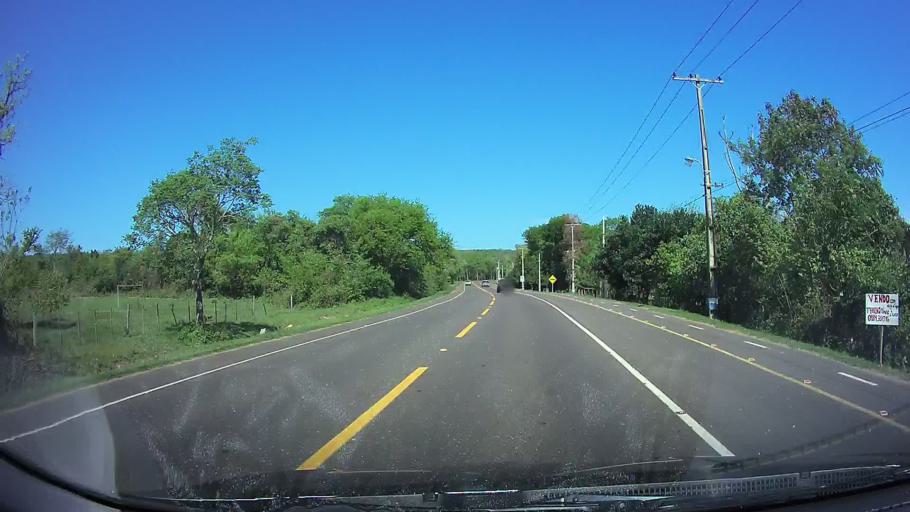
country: PY
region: Cordillera
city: San Bernardino
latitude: -25.2397
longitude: -57.3274
